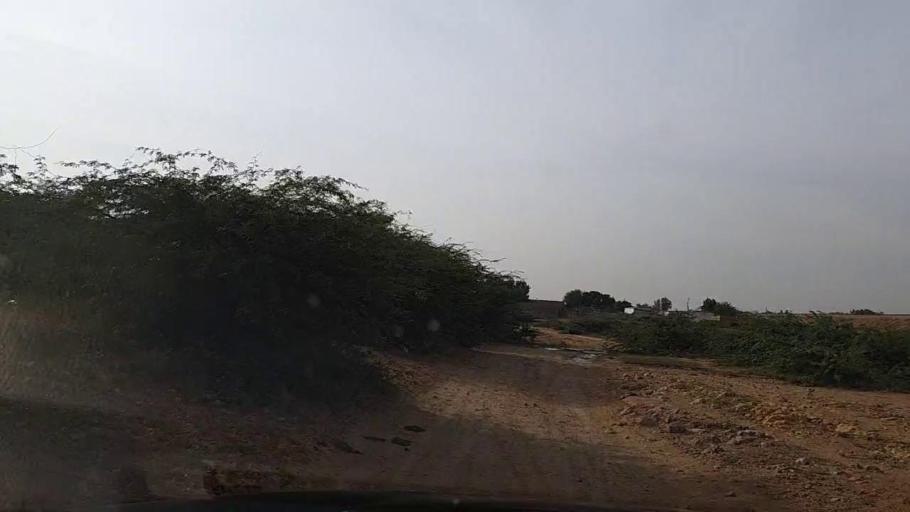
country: PK
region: Sindh
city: Gharo
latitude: 24.7955
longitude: 67.5365
